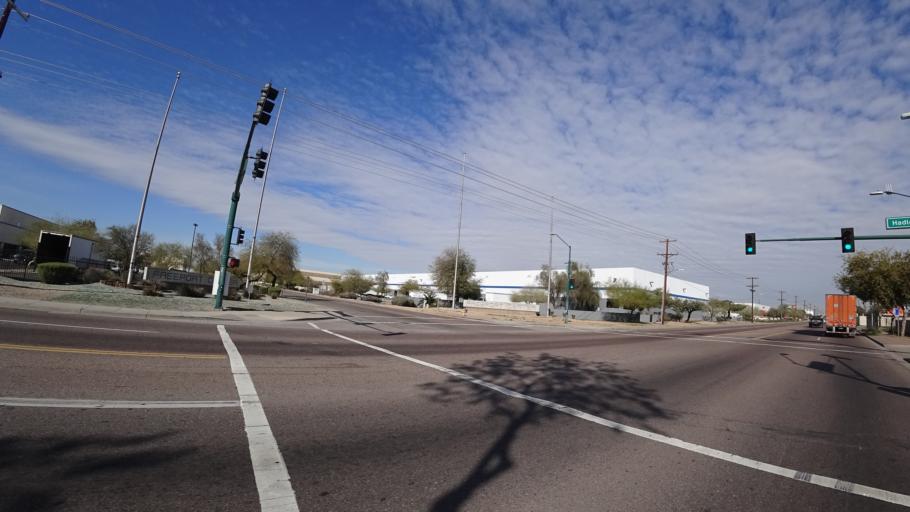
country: US
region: Arizona
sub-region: Maricopa County
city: Laveen
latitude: 33.4395
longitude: -112.1692
